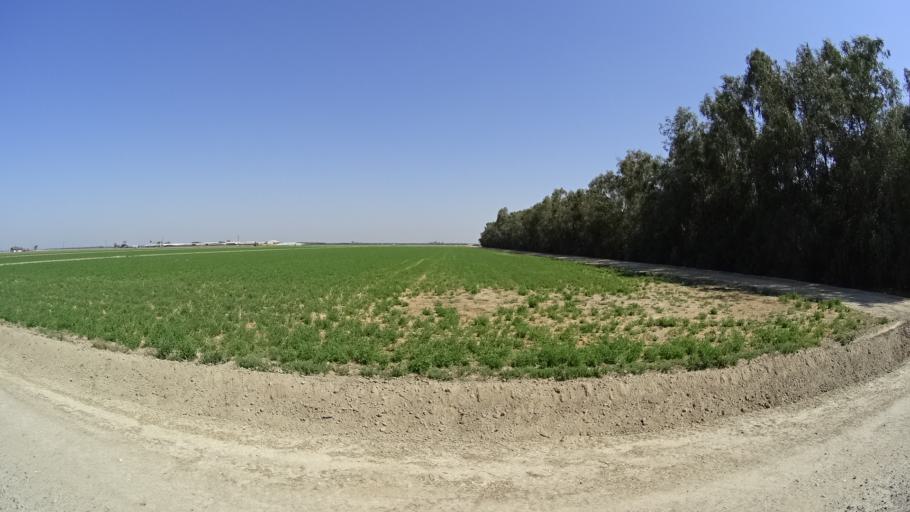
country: US
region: California
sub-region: Kings County
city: Hanford
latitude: 36.3722
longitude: -119.5383
